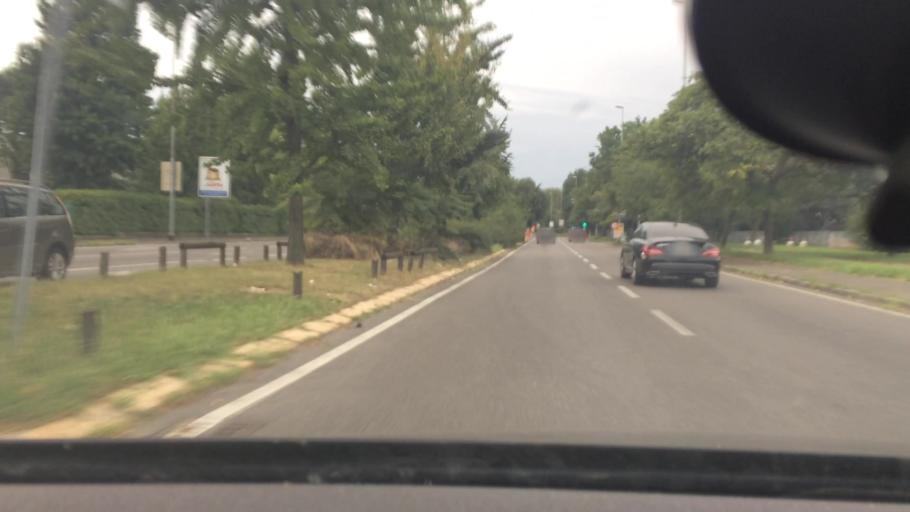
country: IT
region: Lombardy
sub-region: Citta metropolitana di Milano
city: Cinisello Balsamo
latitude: 45.5516
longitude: 9.2030
